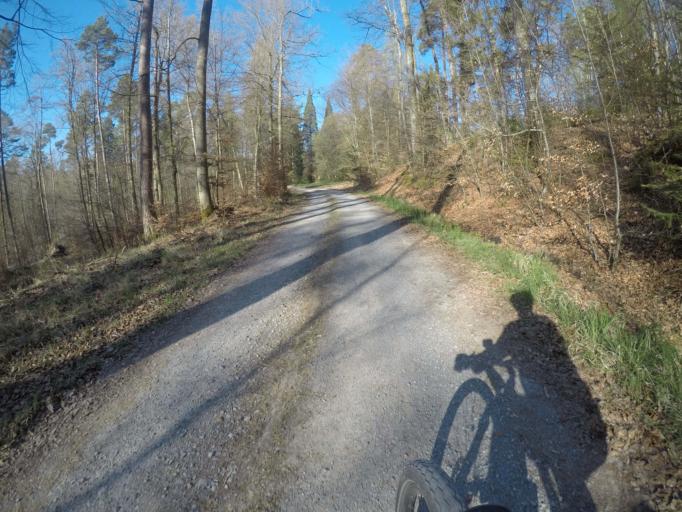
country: DE
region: Baden-Wuerttemberg
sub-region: Regierungsbezirk Stuttgart
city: Waldenbuch
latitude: 48.6082
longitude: 9.1482
